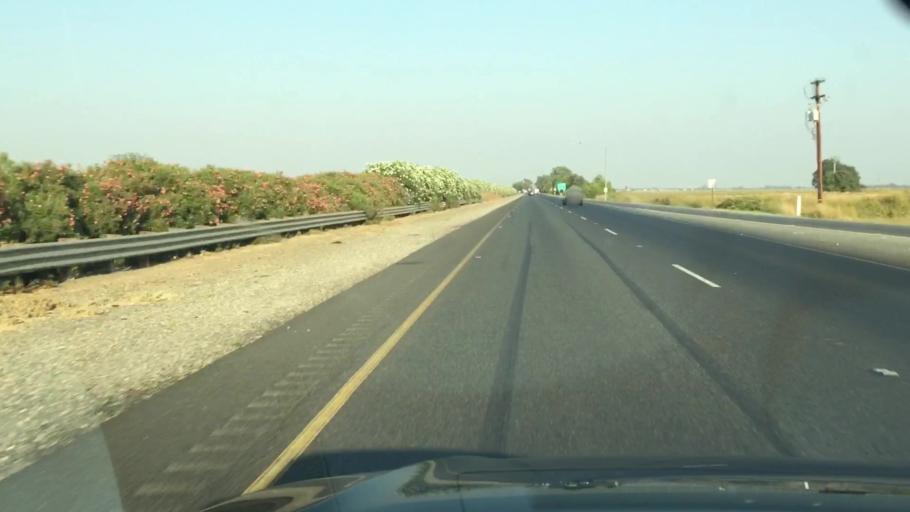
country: US
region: California
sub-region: Yolo County
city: West Sacramento
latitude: 38.6720
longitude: -121.6097
